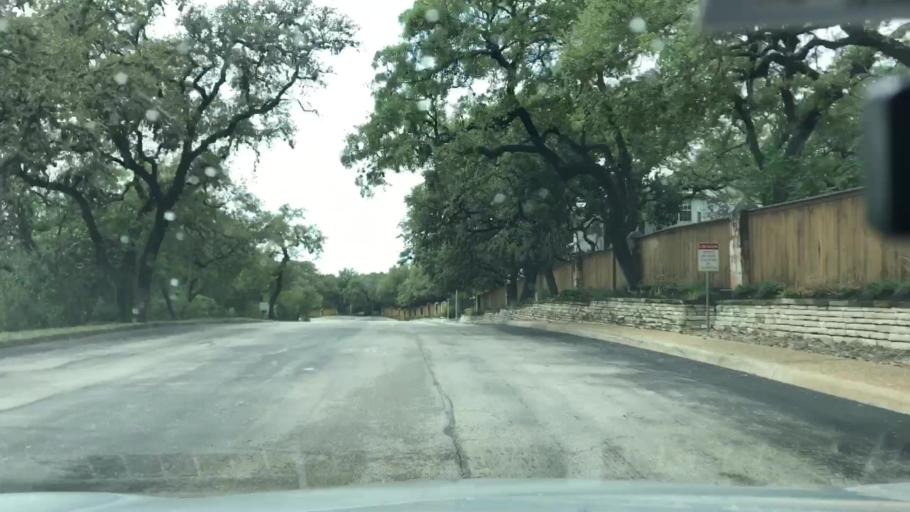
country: US
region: Texas
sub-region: Bexar County
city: Shavano Park
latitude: 29.5993
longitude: -98.5345
